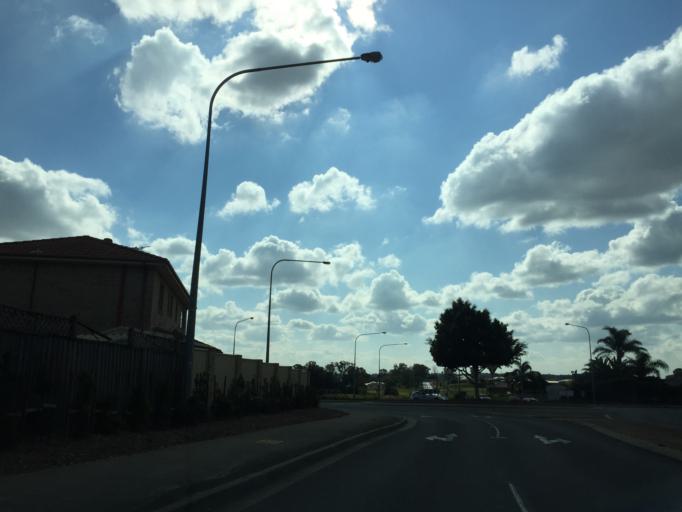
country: AU
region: New South Wales
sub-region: Blacktown
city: Quakers Hill
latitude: -33.7135
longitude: 150.8931
